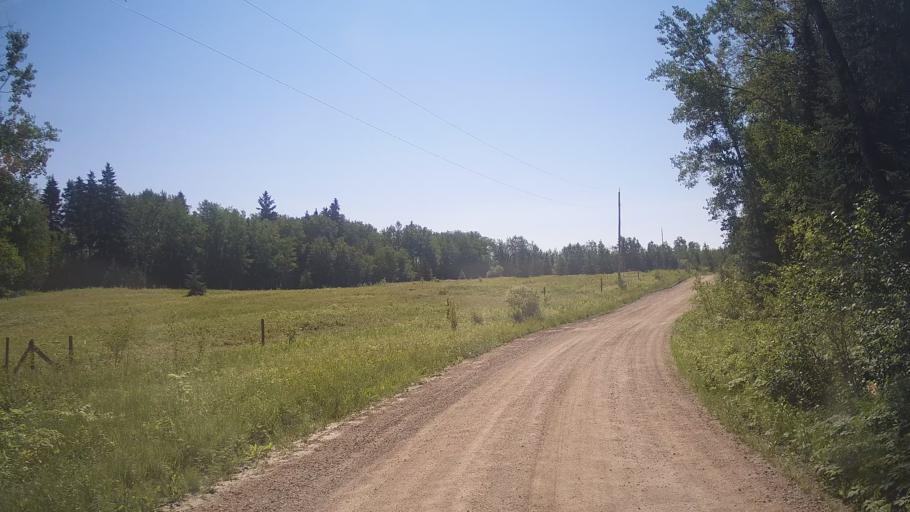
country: CA
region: Ontario
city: Dryden
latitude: 49.8176
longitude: -93.3314
